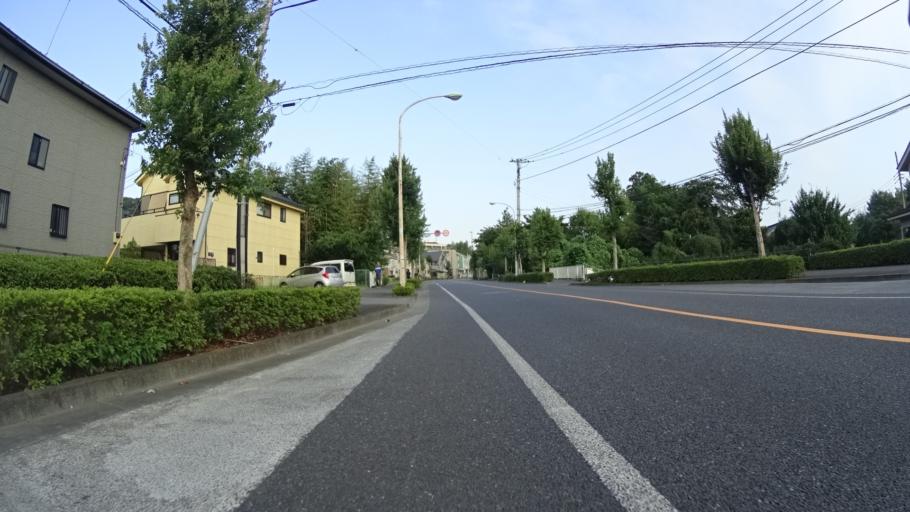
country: JP
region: Tokyo
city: Ome
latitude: 35.7742
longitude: 139.2827
